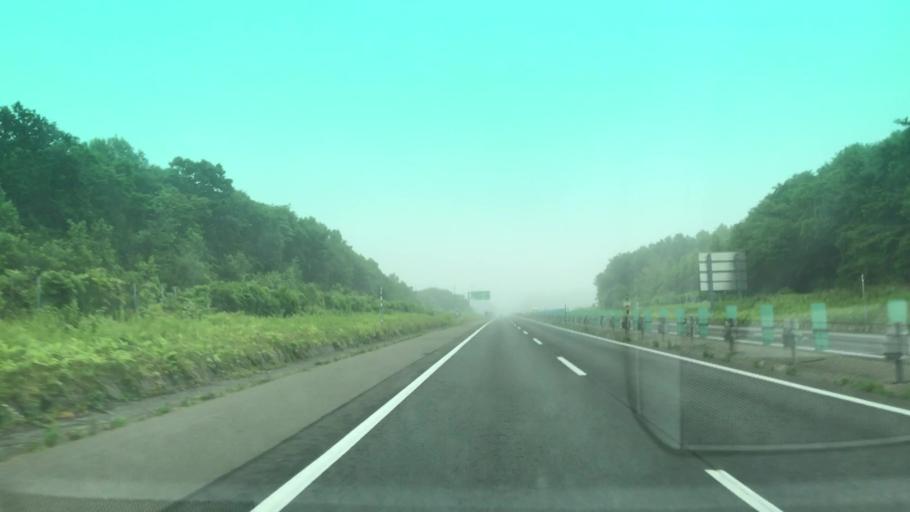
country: JP
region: Hokkaido
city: Chitose
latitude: 42.8220
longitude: 141.6168
